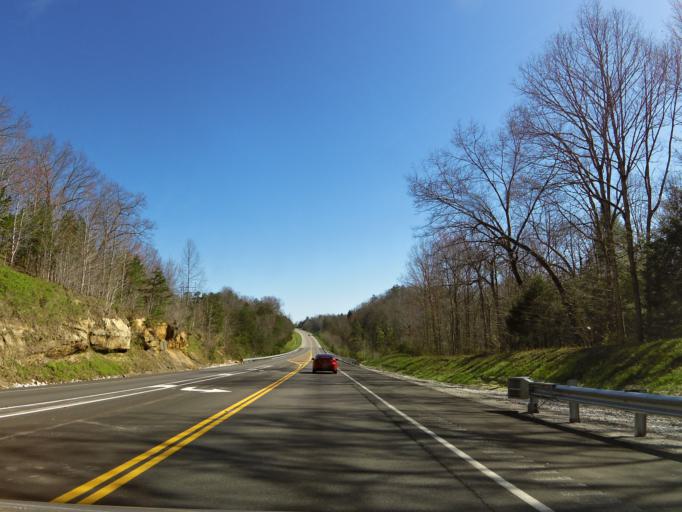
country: US
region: Kentucky
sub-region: McCreary County
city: Whitley City
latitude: 36.7143
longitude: -84.4644
